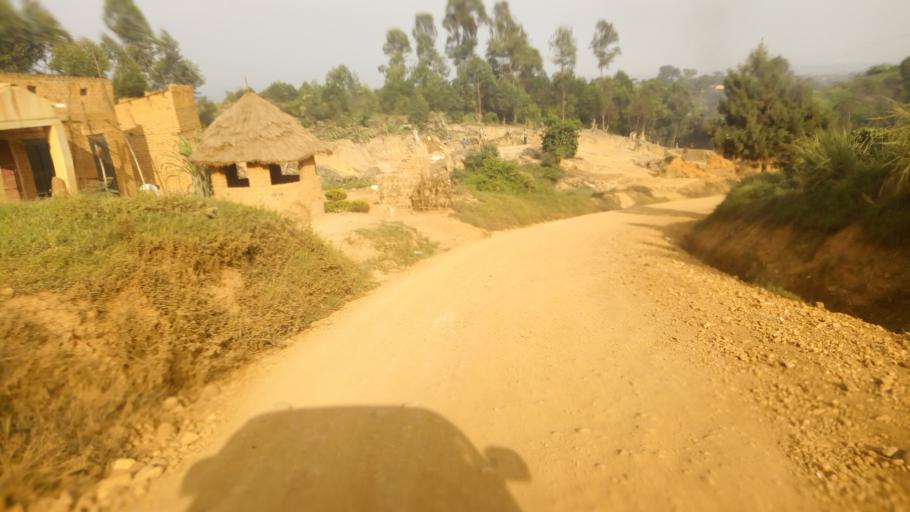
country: UG
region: Western Region
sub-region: Kanungu District
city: Ntungamo
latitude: -0.8350
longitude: 29.6789
